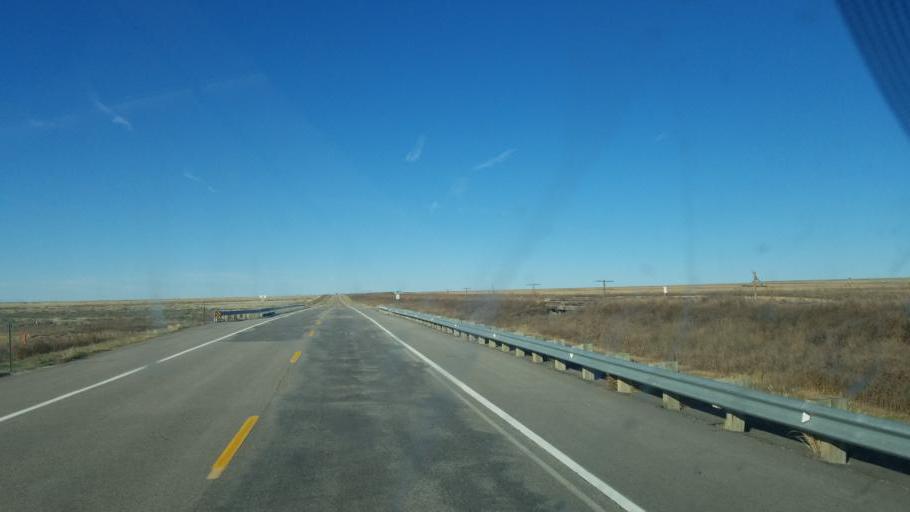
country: US
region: Colorado
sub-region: Crowley County
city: Ordway
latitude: 38.2703
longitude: -103.4801
